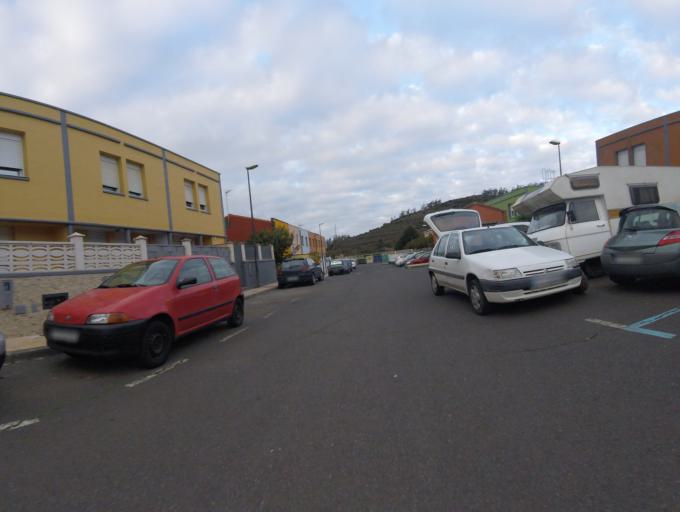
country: ES
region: Canary Islands
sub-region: Provincia de Santa Cruz de Tenerife
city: La Laguna
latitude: 28.4547
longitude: -16.3615
